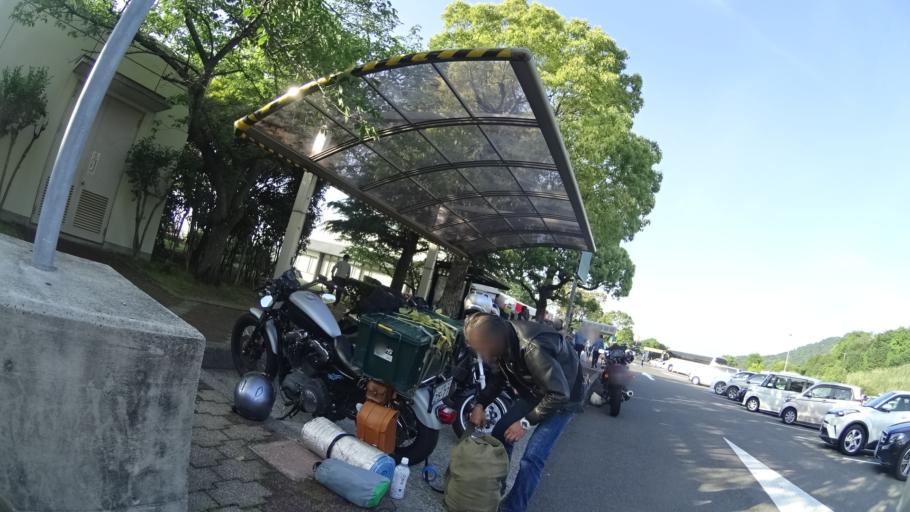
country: JP
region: Ehime
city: Kawanoecho
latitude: 34.0568
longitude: 133.6367
